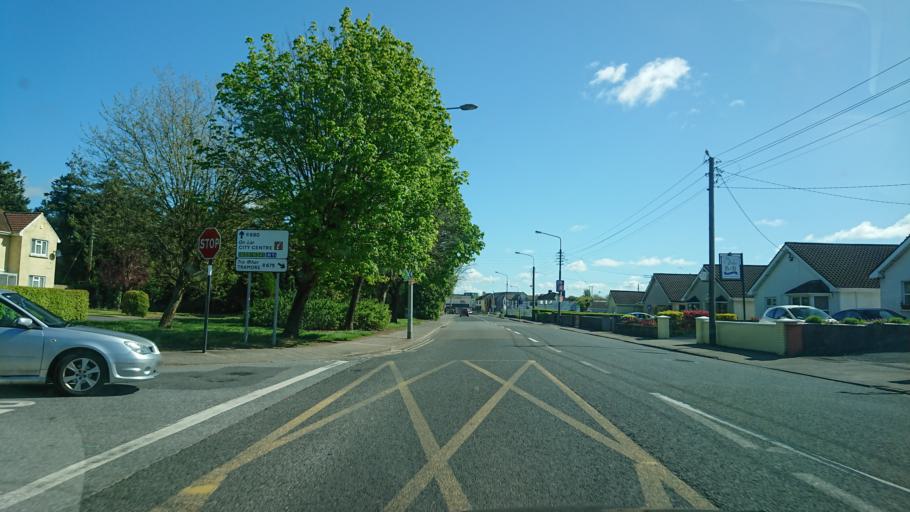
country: IE
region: Munster
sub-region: Waterford
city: Waterford
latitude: 52.2504
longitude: -7.1195
